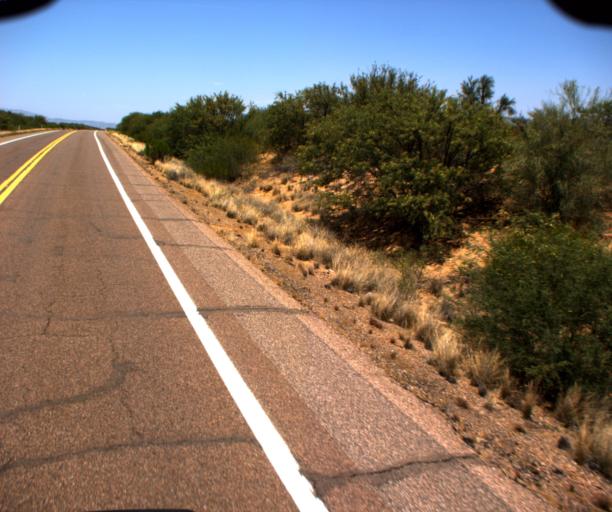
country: US
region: Arizona
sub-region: Gila County
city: Tonto Basin
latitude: 33.7916
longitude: -111.2670
